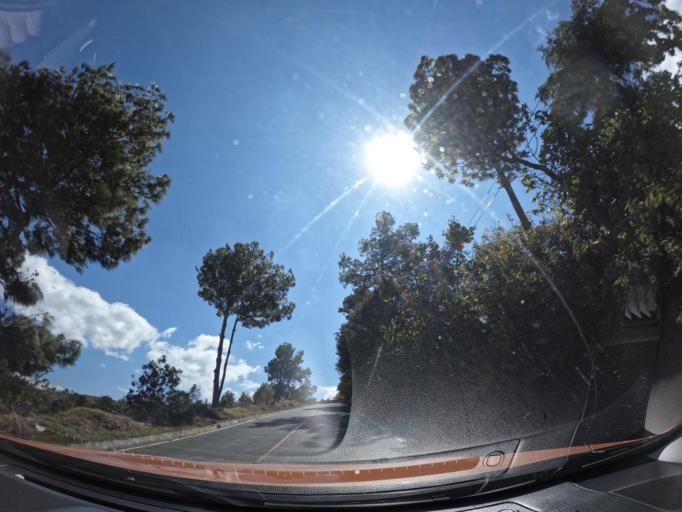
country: GT
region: Chimaltenango
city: Patzun
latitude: 14.6708
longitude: -91.0569
